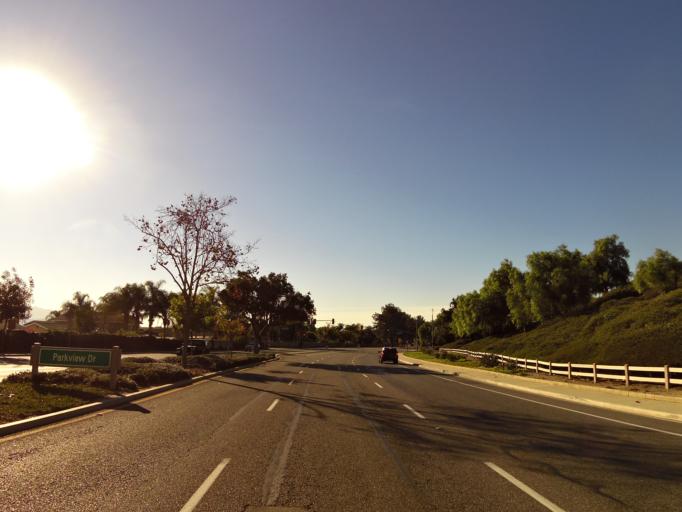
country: US
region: California
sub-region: Ventura County
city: Thousand Oaks
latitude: 34.2119
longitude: -118.8342
